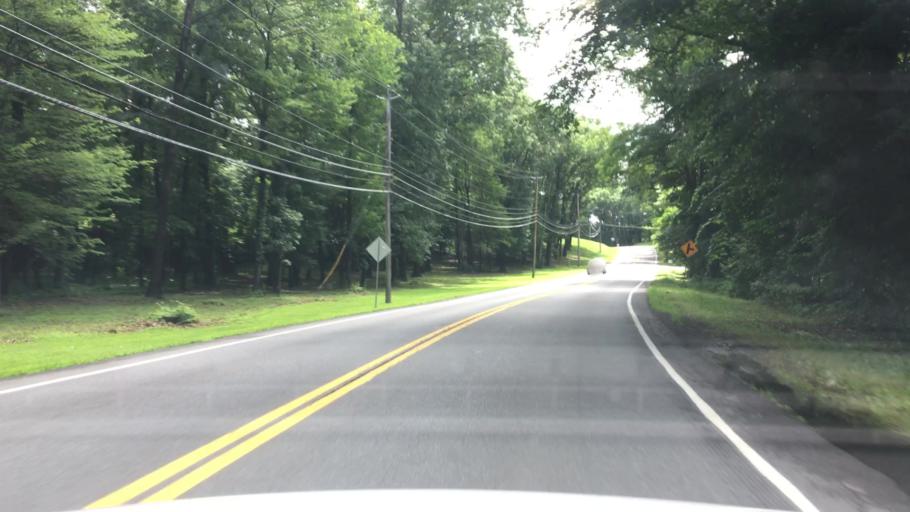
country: US
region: New York
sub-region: Albany County
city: Colonie
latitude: 42.7422
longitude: -73.8352
